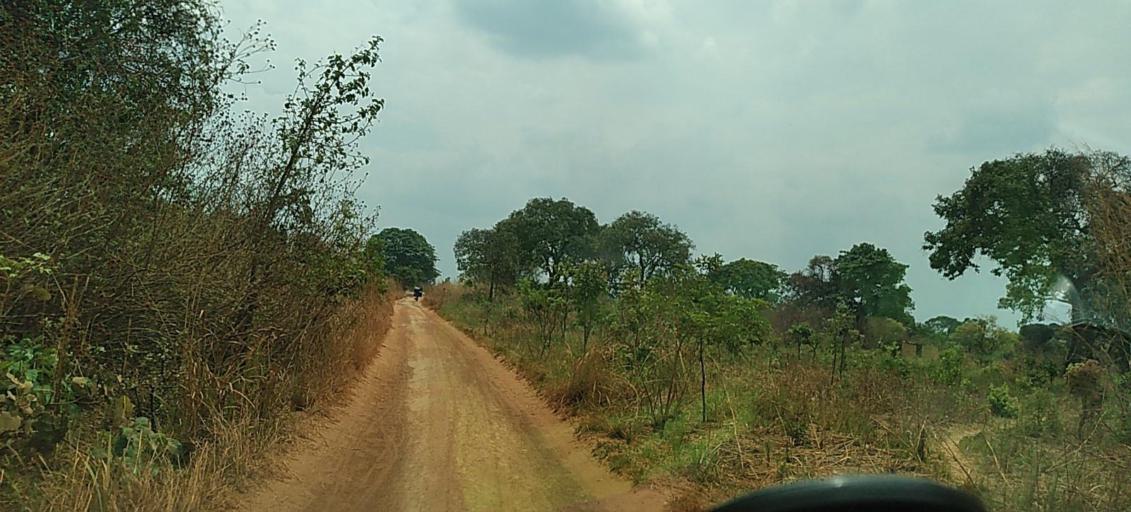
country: ZM
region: North-Western
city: Kansanshi
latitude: -12.0579
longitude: 26.3465
